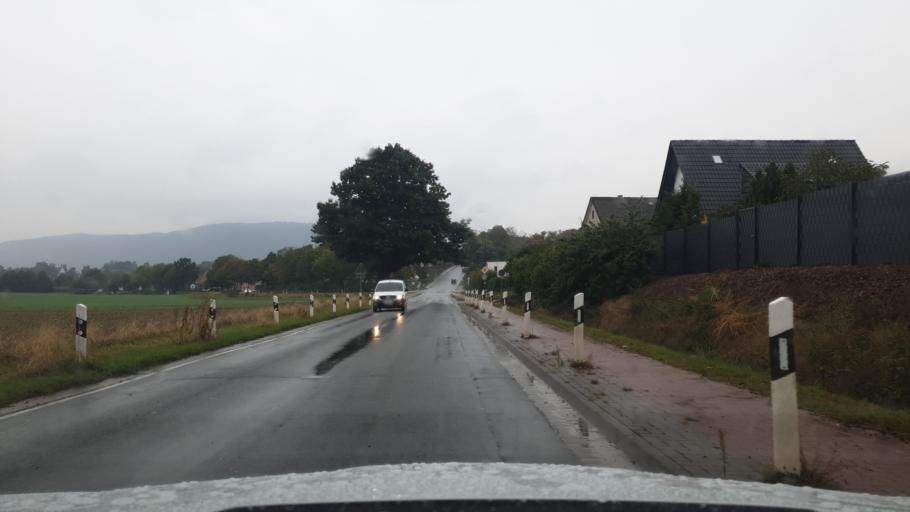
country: DE
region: North Rhine-Westphalia
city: Porta Westfalica
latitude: 52.2216
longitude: 8.9175
